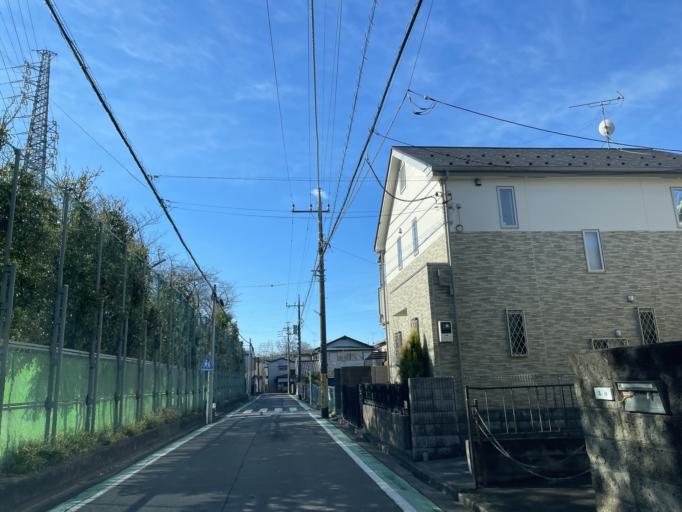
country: JP
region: Saitama
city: Tokorozawa
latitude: 35.7831
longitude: 139.4474
